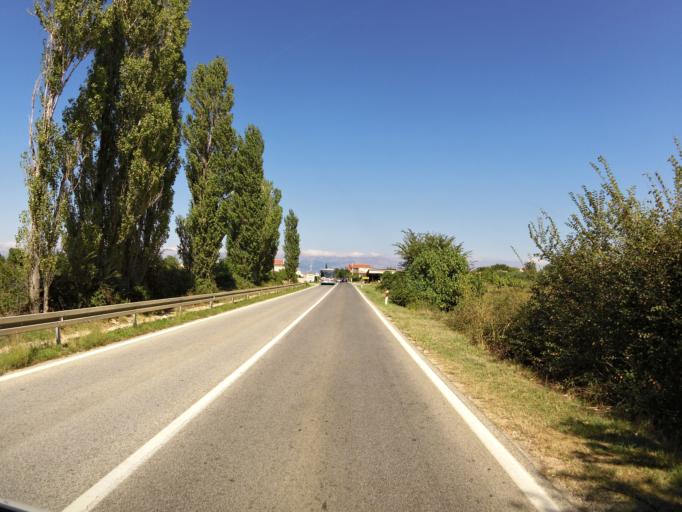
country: HR
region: Zadarska
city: Policnik
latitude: 44.1851
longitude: 15.3952
